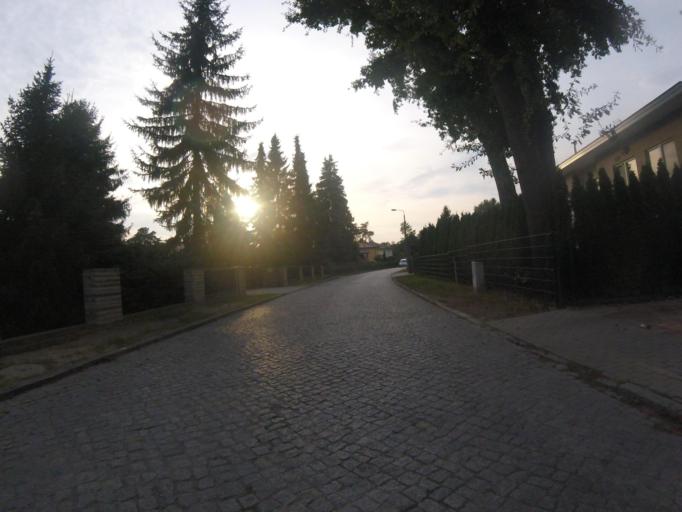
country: DE
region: Brandenburg
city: Zeuthen
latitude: 52.3535
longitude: 13.6173
